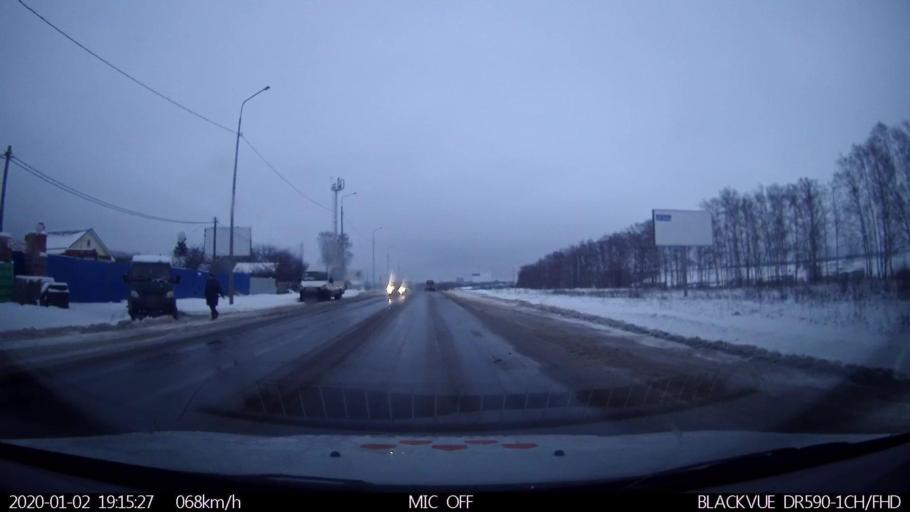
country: RU
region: Nizjnij Novgorod
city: Burevestnik
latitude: 56.2104
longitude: 43.8845
